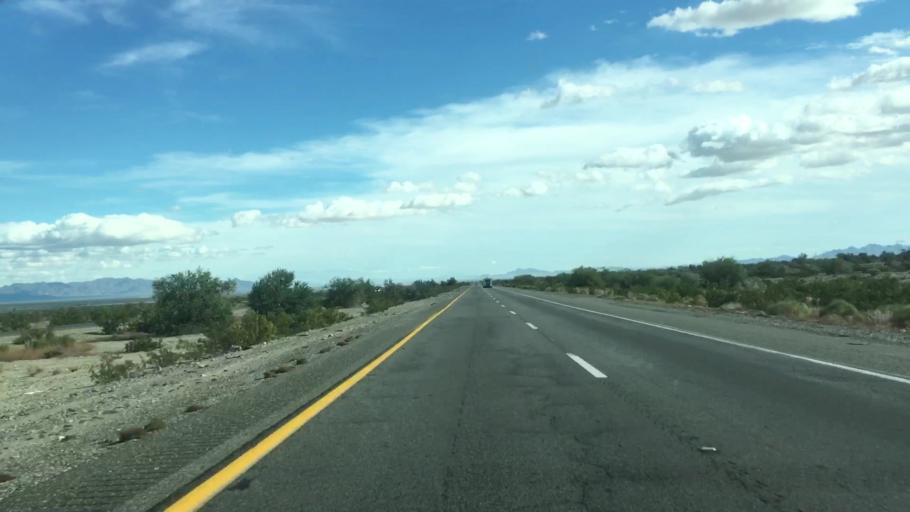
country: US
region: California
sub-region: Riverside County
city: Mesa Verde
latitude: 33.6759
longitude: -115.2220
